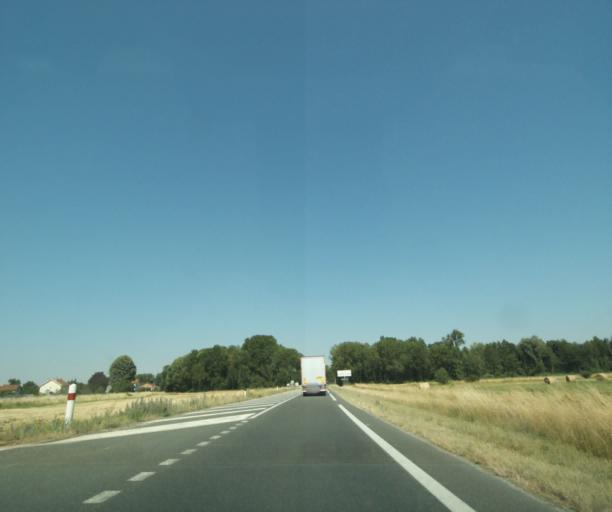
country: FR
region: Champagne-Ardenne
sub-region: Departement de la Haute-Marne
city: Villiers-en-Lieu
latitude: 48.6461
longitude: 4.8771
